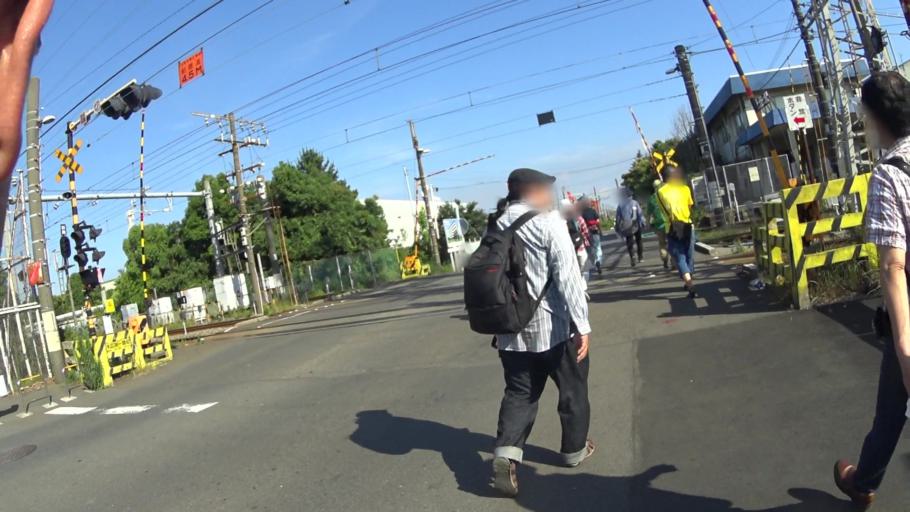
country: JP
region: Kanagawa
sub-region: Kawasaki-shi
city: Kawasaki
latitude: 35.4978
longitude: 139.6960
